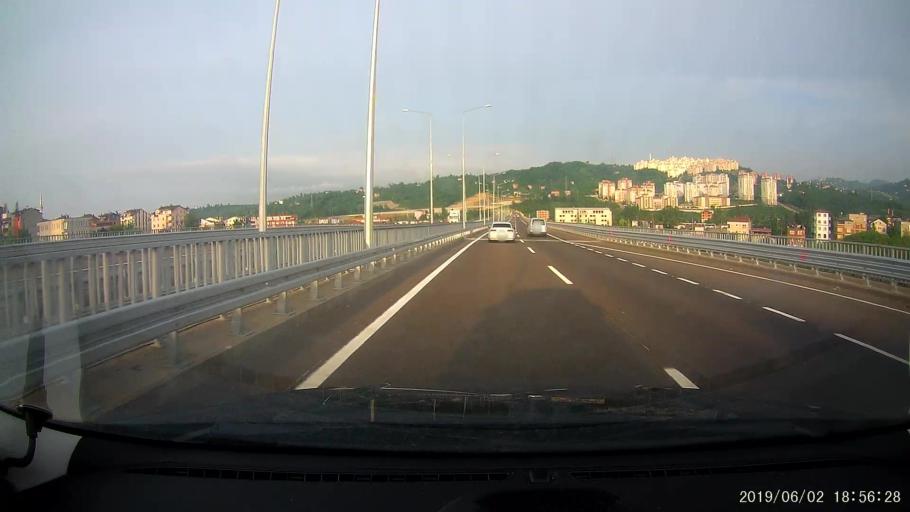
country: TR
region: Ordu
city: Ordu
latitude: 40.9558
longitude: 37.8917
